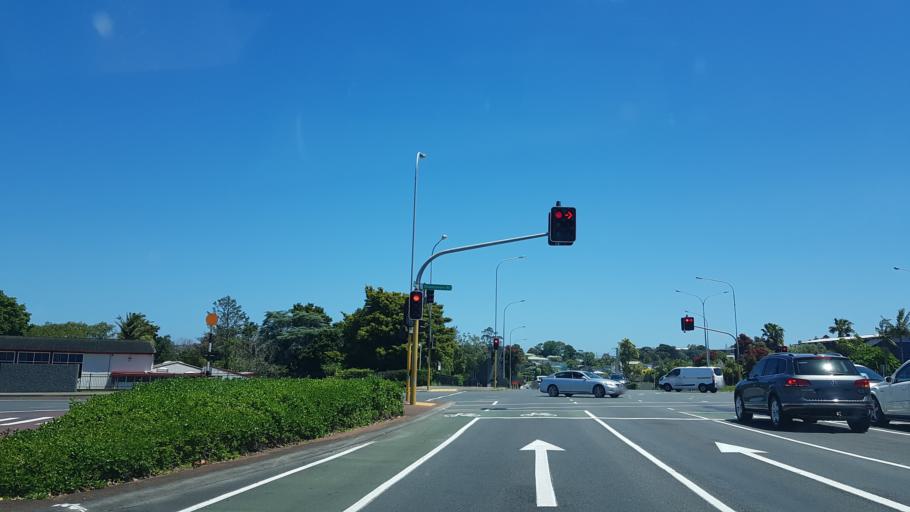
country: NZ
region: Auckland
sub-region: Auckland
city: North Shore
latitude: -36.7831
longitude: 174.7533
